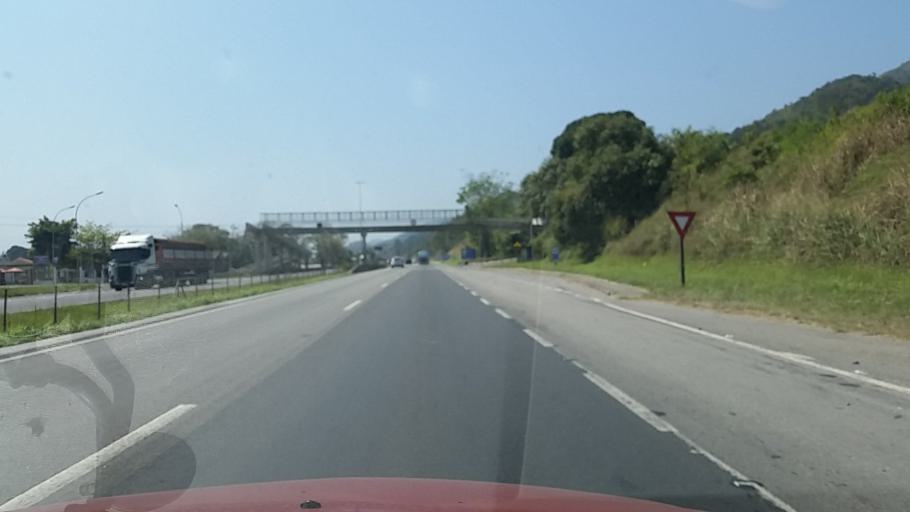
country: BR
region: Sao Paulo
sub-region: Miracatu
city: Miracatu
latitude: -24.2876
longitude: -47.4553
